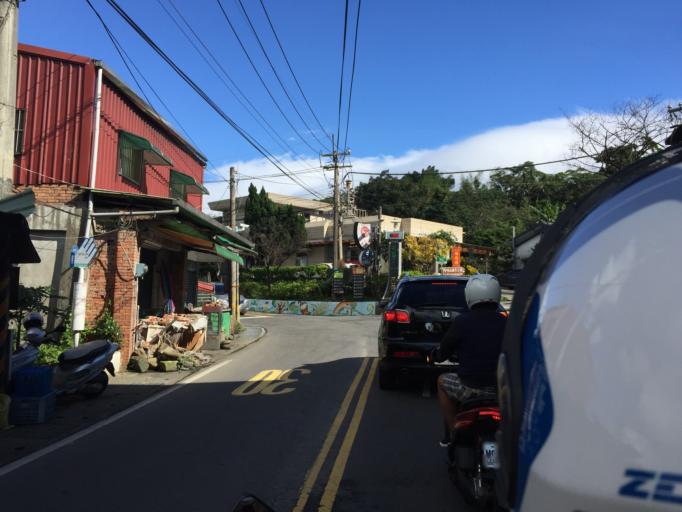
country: TW
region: Taipei
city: Taipei
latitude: 25.2046
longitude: 121.5015
